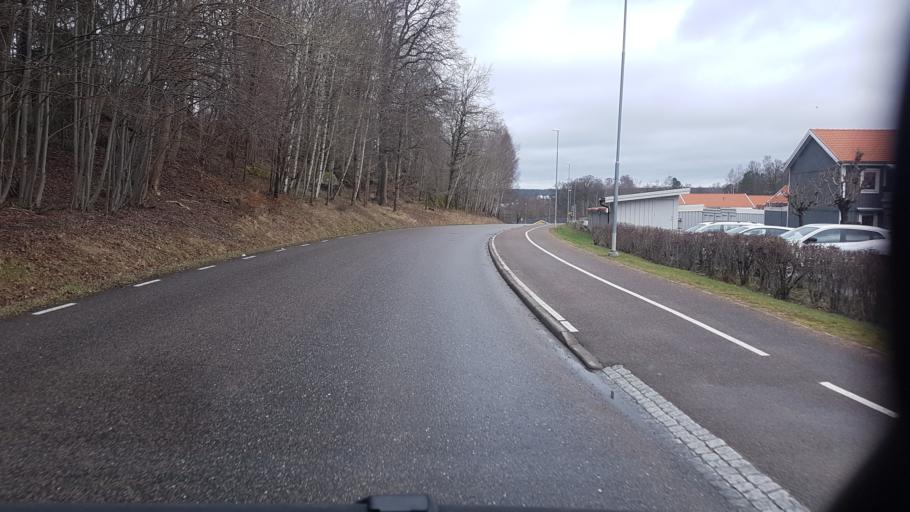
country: SE
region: Vaestra Goetaland
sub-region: Lerums Kommun
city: Lerum
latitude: 57.7530
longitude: 12.2581
